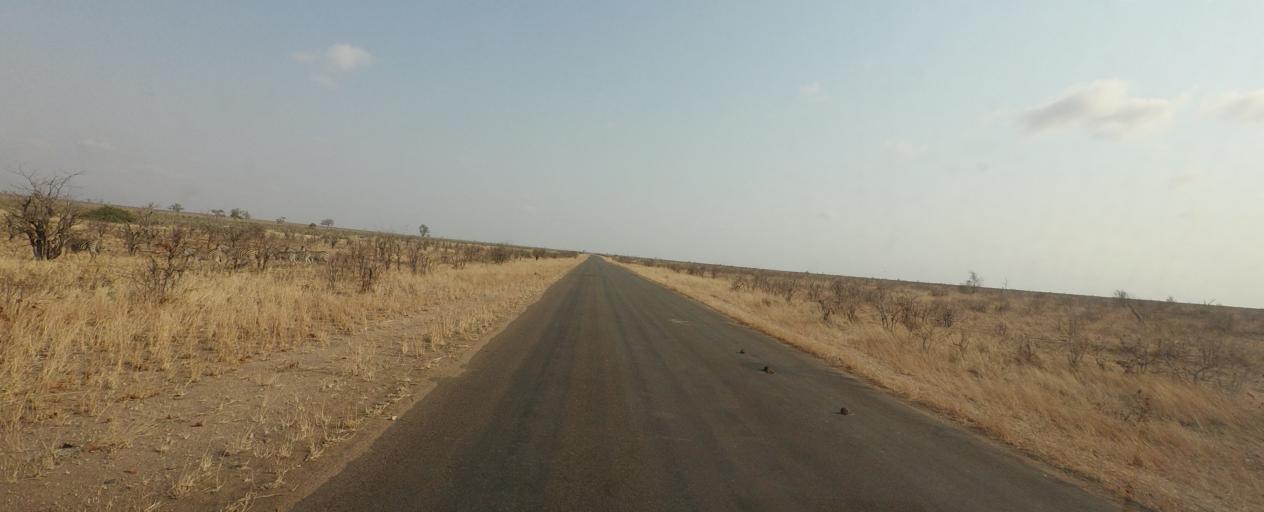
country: ZA
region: Limpopo
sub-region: Vhembe District Municipality
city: Mutale
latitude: -22.9510
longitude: 31.2883
